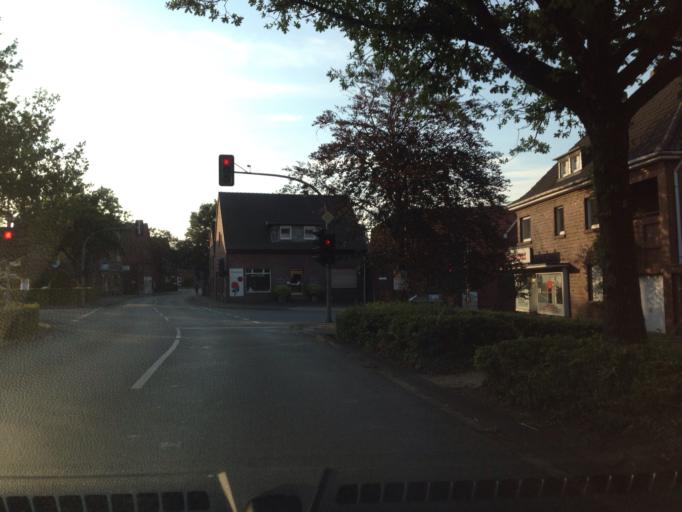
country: DE
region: North Rhine-Westphalia
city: Ludinghausen
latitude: 51.7625
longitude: 7.3948
